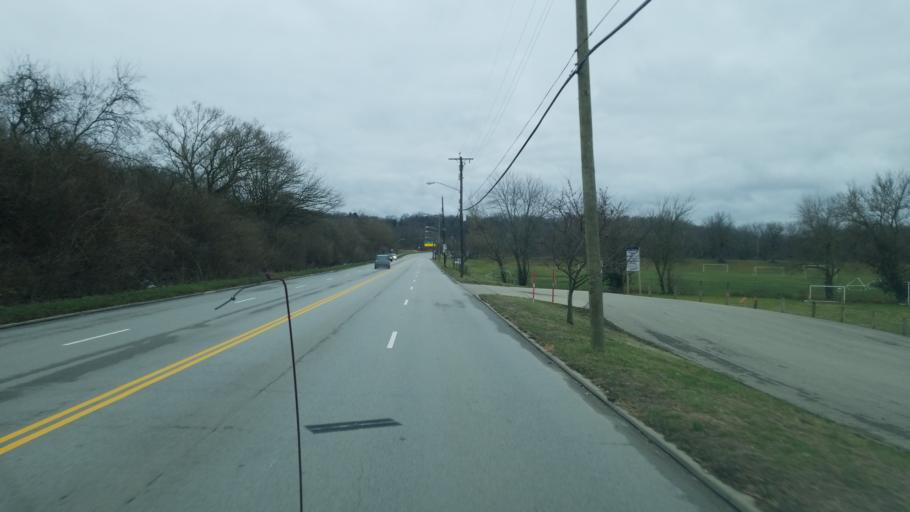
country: US
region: Kentucky
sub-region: Campbell County
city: Fort Thomas
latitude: 39.0899
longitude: -84.4251
